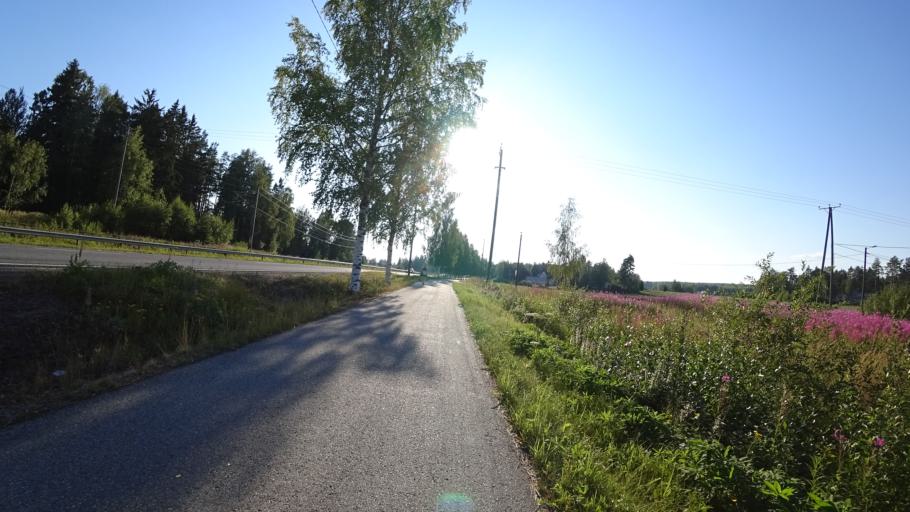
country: FI
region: Pirkanmaa
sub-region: Tampere
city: Nokia
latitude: 61.4670
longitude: 23.4080
